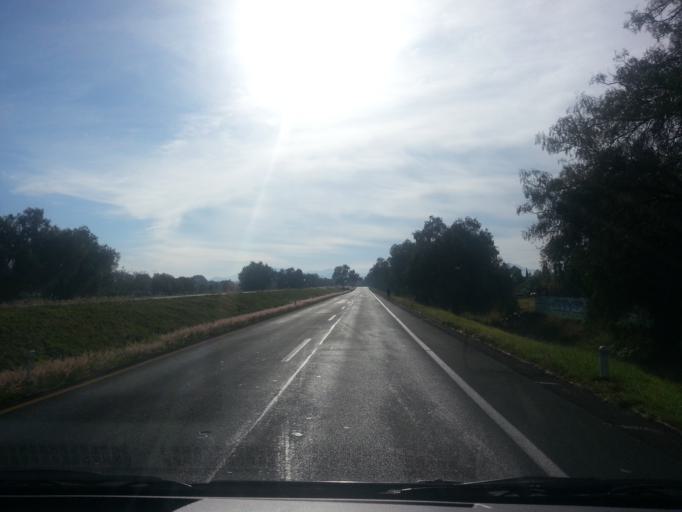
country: MX
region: Mexico
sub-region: Acolman de Nezahualcoyotl
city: Prados de San Juan
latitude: 19.6210
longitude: -98.9671
